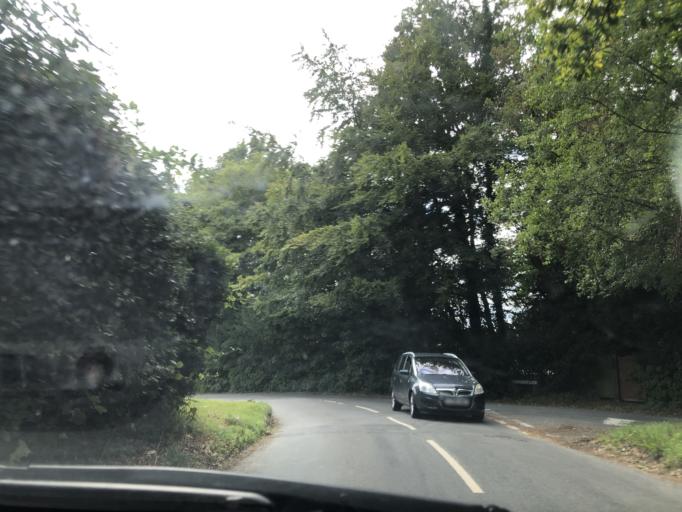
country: GB
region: England
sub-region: East Sussex
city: Forest Row
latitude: 51.0828
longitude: 0.0716
